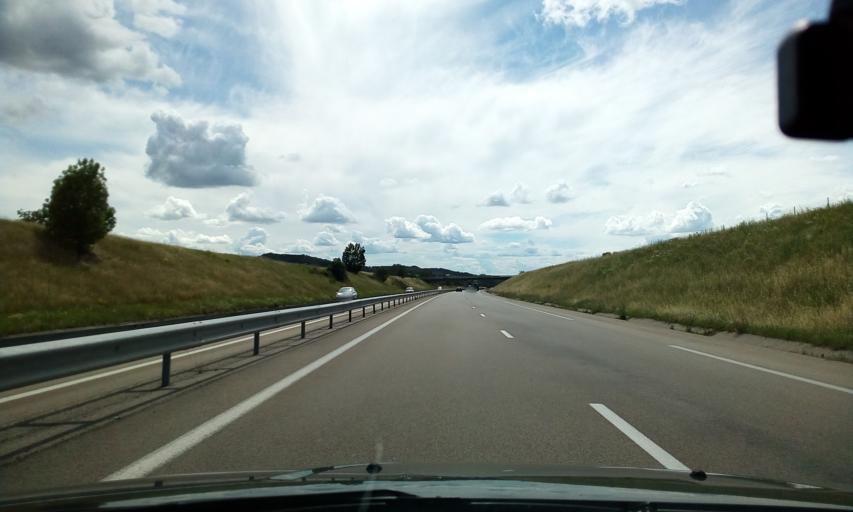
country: FR
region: Rhone-Alpes
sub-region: Departement de l'Isere
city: Saint-Lattier
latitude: 45.0537
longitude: 5.1815
